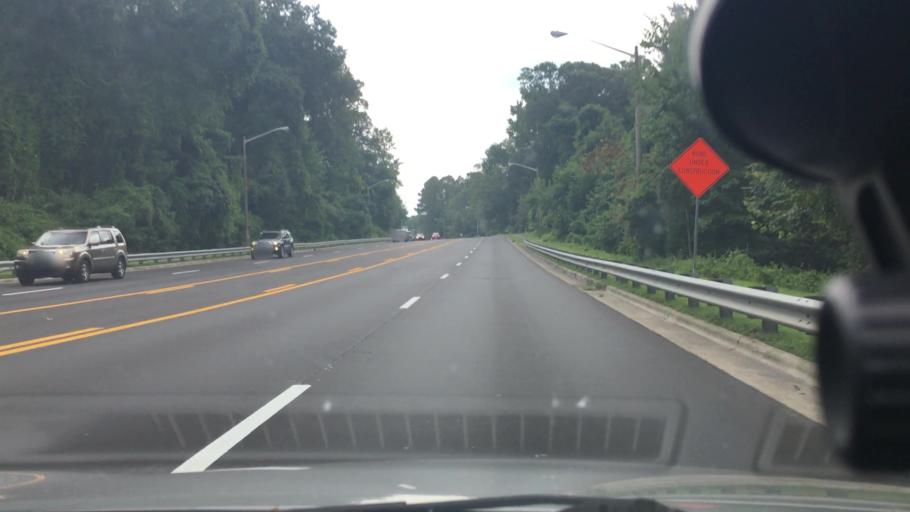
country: US
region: North Carolina
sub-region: Pitt County
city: Greenville
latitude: 35.5950
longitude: -77.3228
